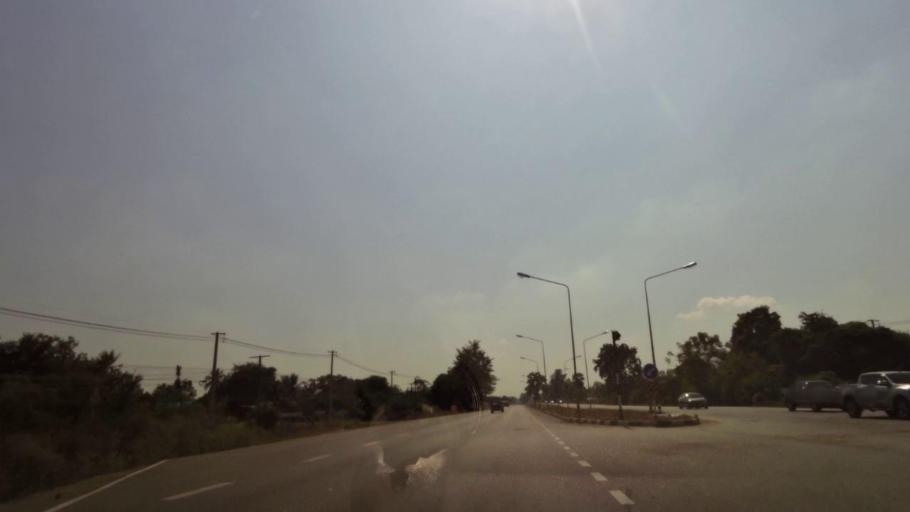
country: TH
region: Phichit
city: Bueng Na Rang
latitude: 16.2644
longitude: 100.1262
